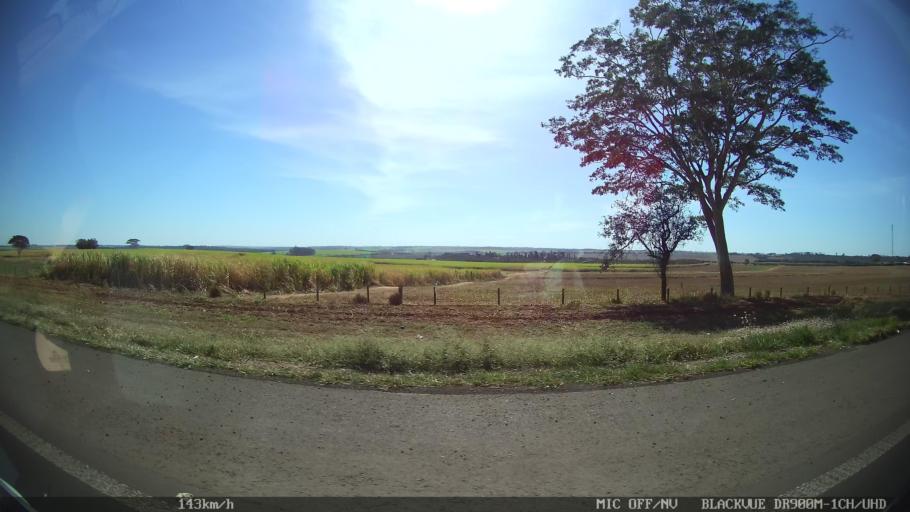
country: BR
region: Sao Paulo
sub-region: Barretos
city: Barretos
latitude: -20.5800
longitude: -48.6882
